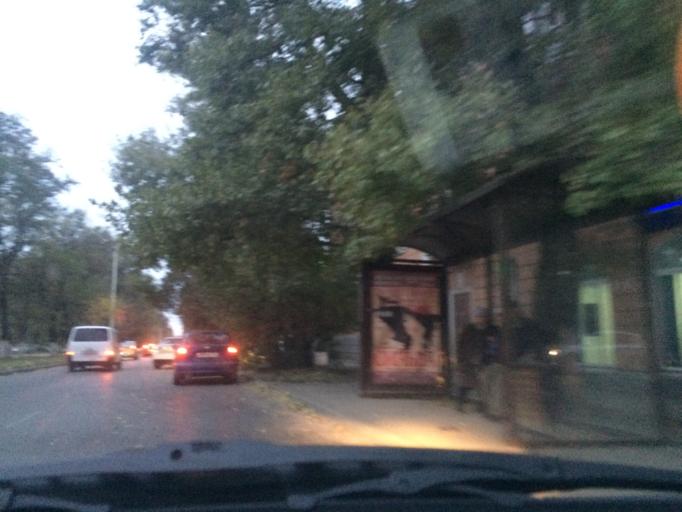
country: RU
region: Rostov
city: Novocherkassk
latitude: 47.4163
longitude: 40.1060
